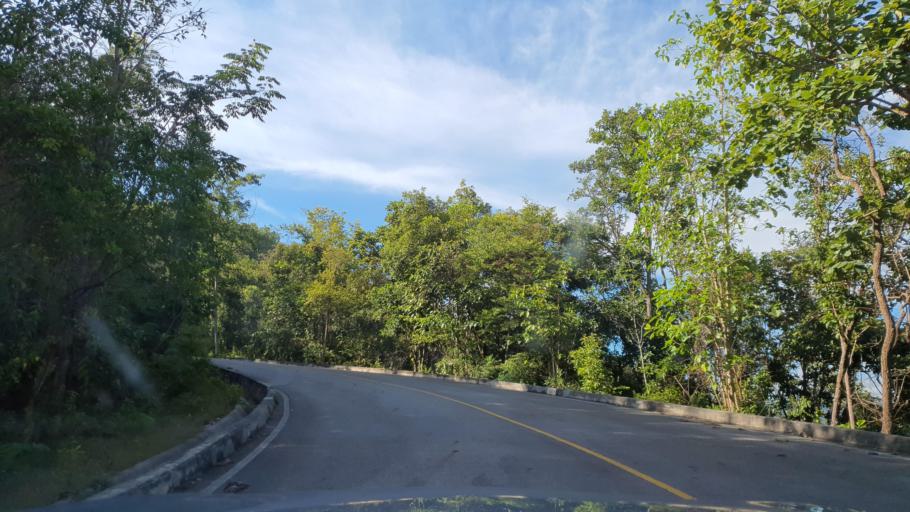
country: TH
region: Chiang Mai
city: Mae On
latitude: 18.7779
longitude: 99.2887
